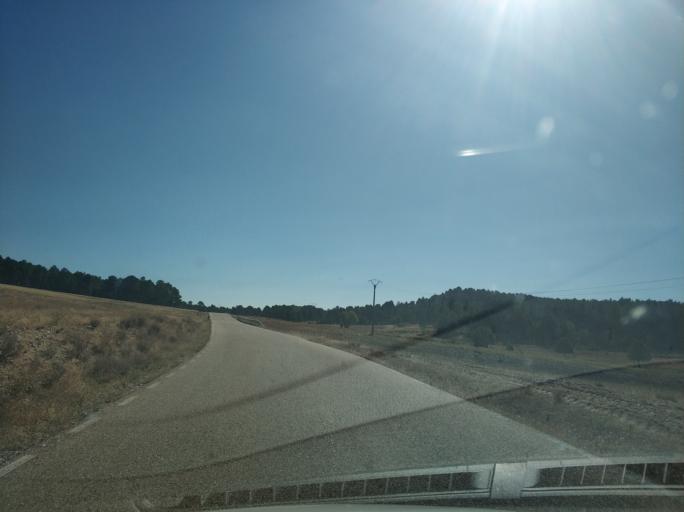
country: ES
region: Castille and Leon
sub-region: Provincia de Soria
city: Espeja de San Marcelino
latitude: 41.7803
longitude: -3.1896
